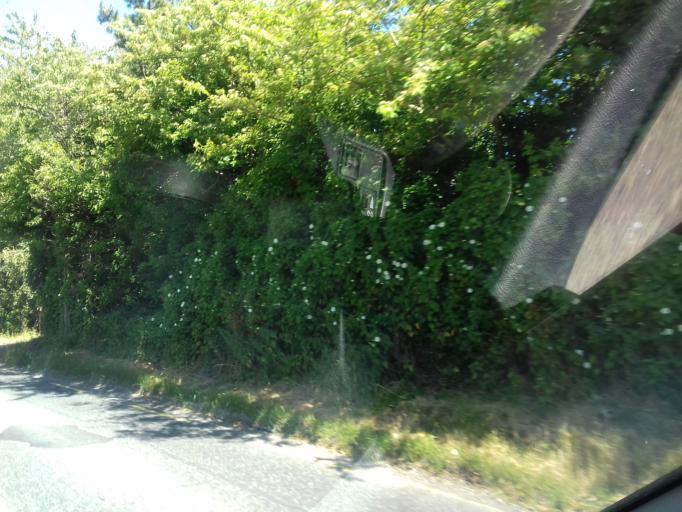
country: IE
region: Leinster
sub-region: Fingal County
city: Swords
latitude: 53.4588
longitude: -6.2676
